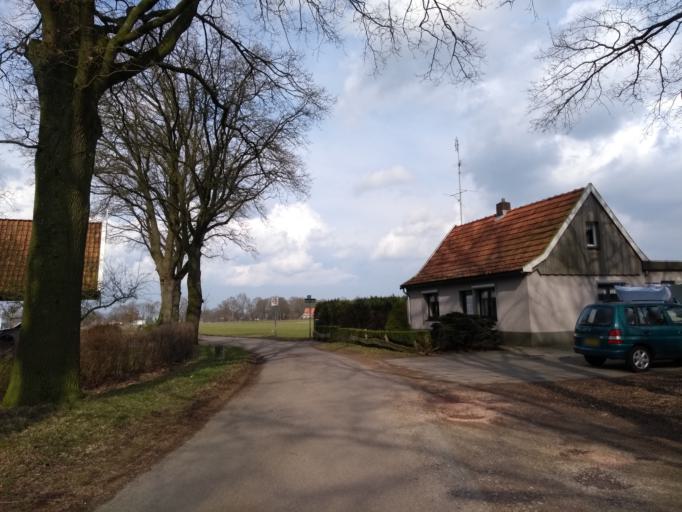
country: NL
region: Overijssel
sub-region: Gemeente Almelo
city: Almelo
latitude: 52.3737
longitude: 6.7125
